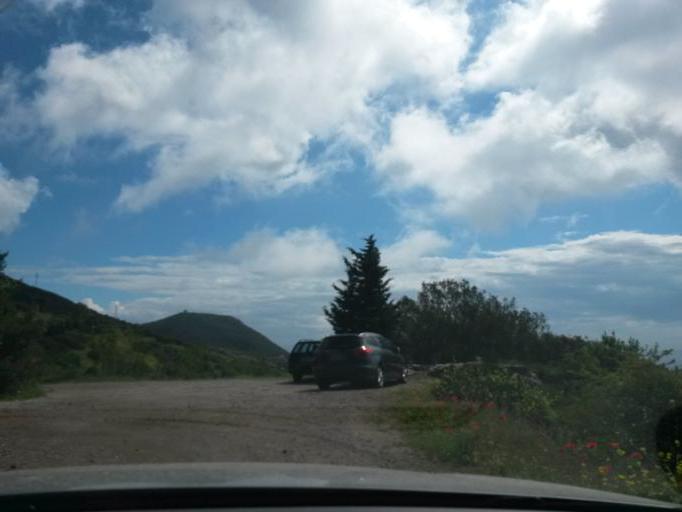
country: IT
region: Tuscany
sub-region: Provincia di Livorno
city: Rio nell'Elba
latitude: 42.8244
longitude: 10.4043
